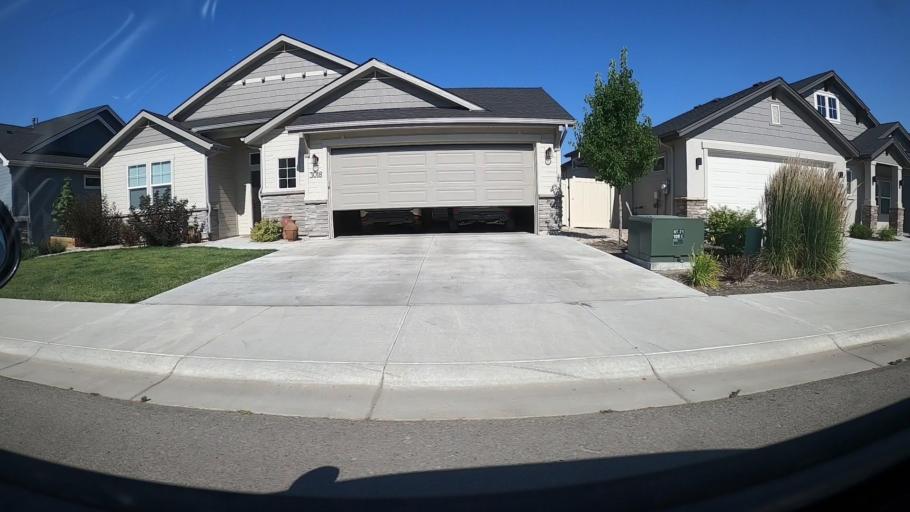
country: US
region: Idaho
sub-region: Ada County
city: Meridian
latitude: 43.6321
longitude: -116.4105
